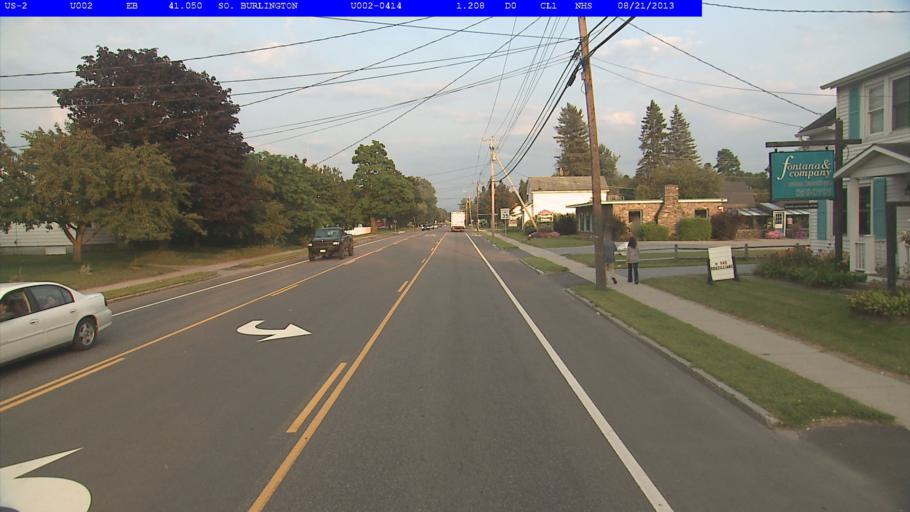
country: US
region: Vermont
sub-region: Chittenden County
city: South Burlington
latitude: 44.4661
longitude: -73.1676
